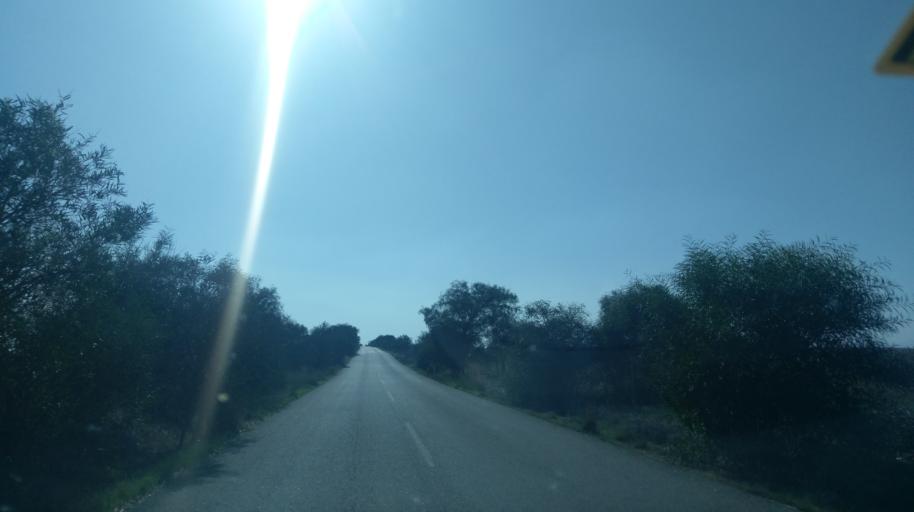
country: CY
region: Larnaka
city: Athienou
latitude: 35.1086
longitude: 33.4974
